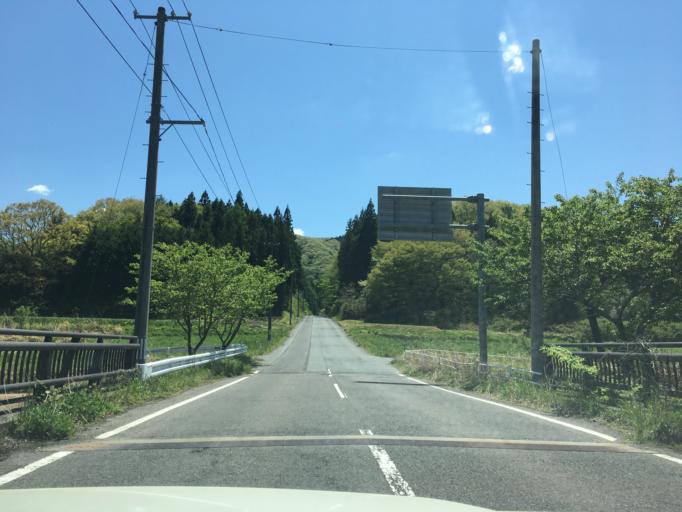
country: JP
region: Fukushima
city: Funehikimachi-funehiki
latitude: 37.3544
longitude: 140.6311
